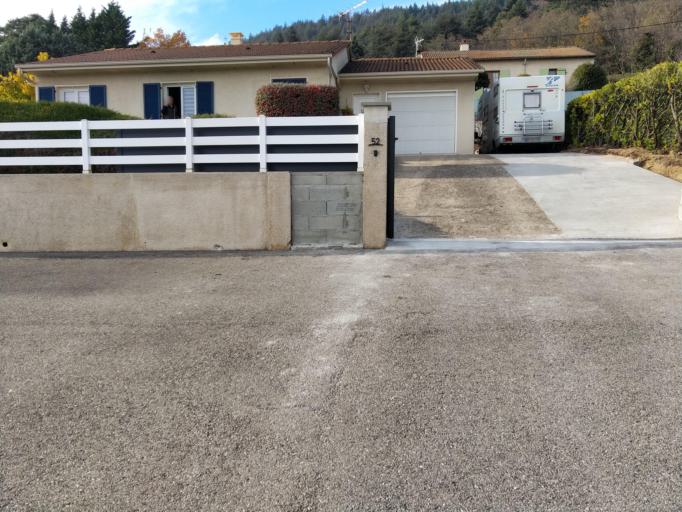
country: FR
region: Rhone-Alpes
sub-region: Departement de l'Ardeche
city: Annonay
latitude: 45.2523
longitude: 4.6543
